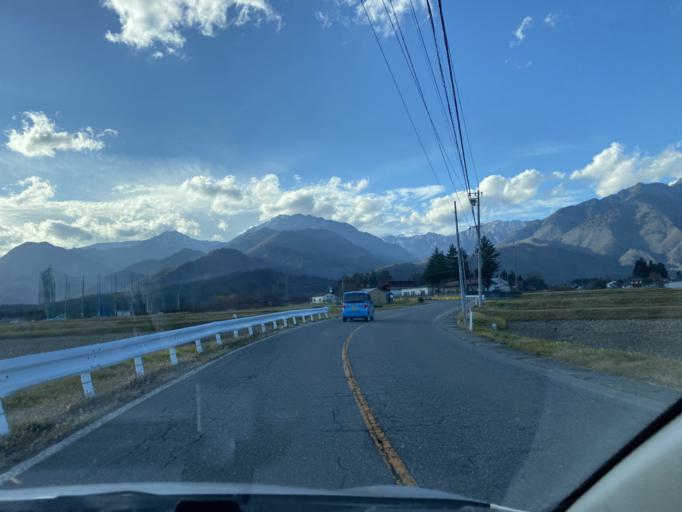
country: JP
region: Nagano
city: Omachi
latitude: 36.5274
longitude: 137.8247
